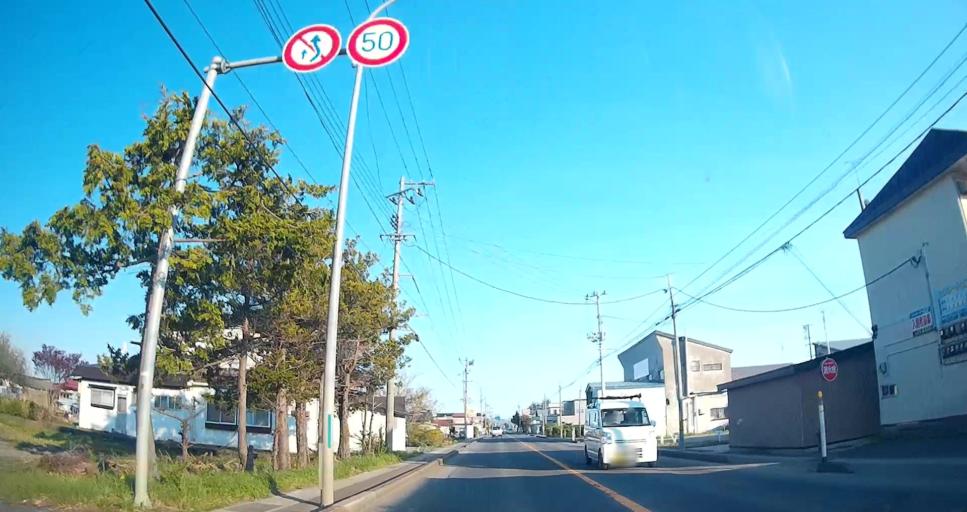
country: JP
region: Aomori
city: Mutsu
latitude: 41.2745
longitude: 141.2149
